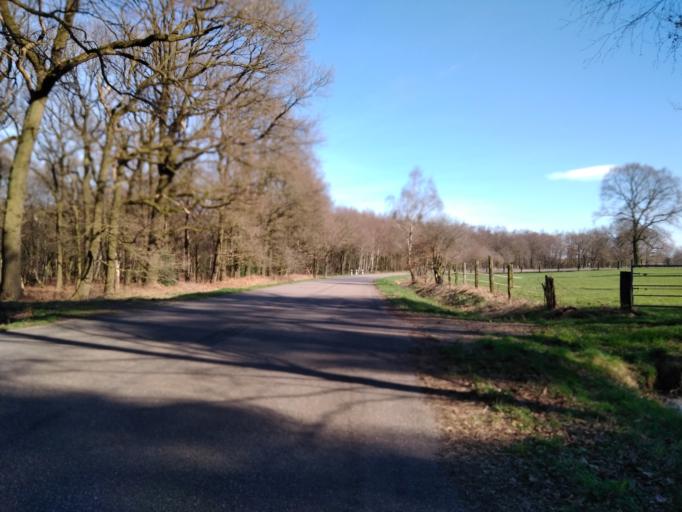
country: DE
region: North Rhine-Westphalia
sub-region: Regierungsbezirk Dusseldorf
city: Hunxe
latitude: 51.6196
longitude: 6.8400
